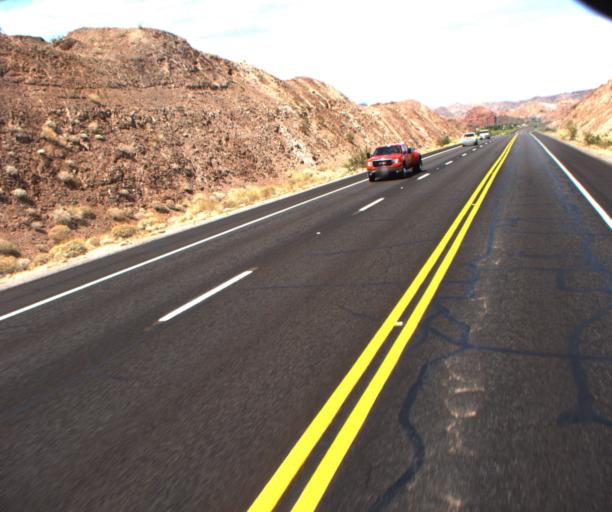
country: US
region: Arizona
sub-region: La Paz County
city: Cienega Springs
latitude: 34.2341
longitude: -114.1786
